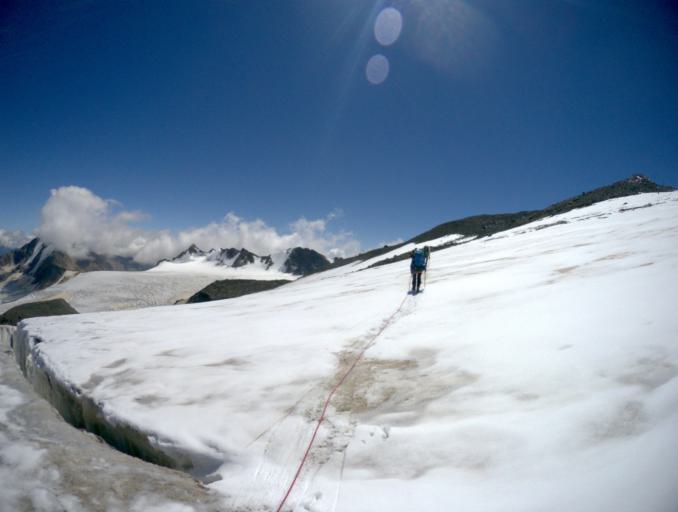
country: RU
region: Kabardino-Balkariya
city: Terskol
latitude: 43.3503
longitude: 42.5040
